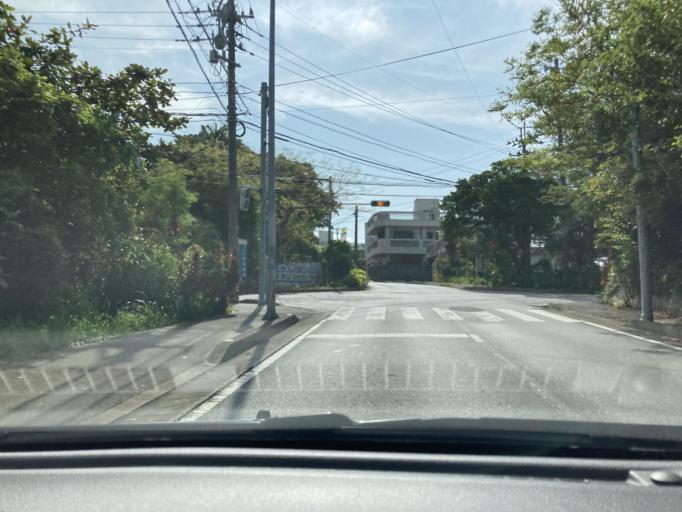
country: JP
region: Okinawa
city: Chatan
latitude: 26.2935
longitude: 127.7962
